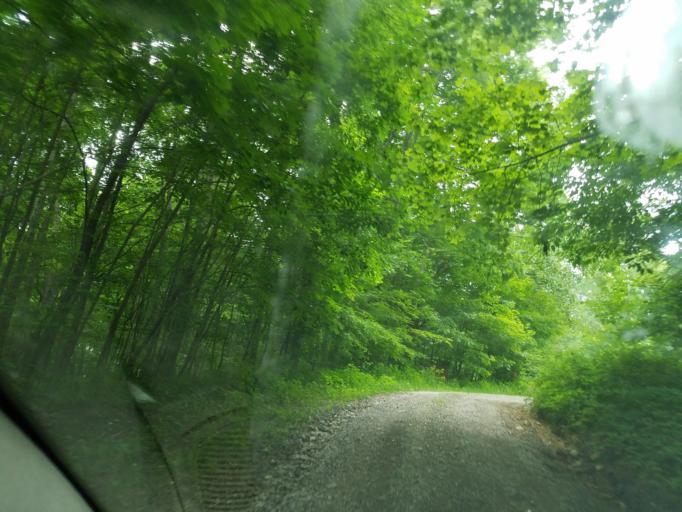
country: US
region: Ohio
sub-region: Sandusky County
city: Bellville
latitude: 40.5974
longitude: -82.5707
